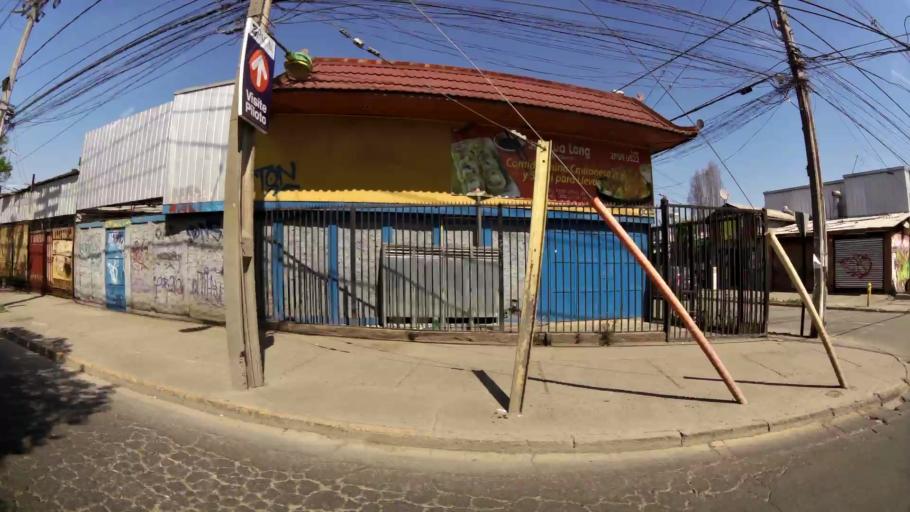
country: CL
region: Santiago Metropolitan
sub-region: Provincia de Santiago
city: Lo Prado
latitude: -33.3640
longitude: -70.7347
